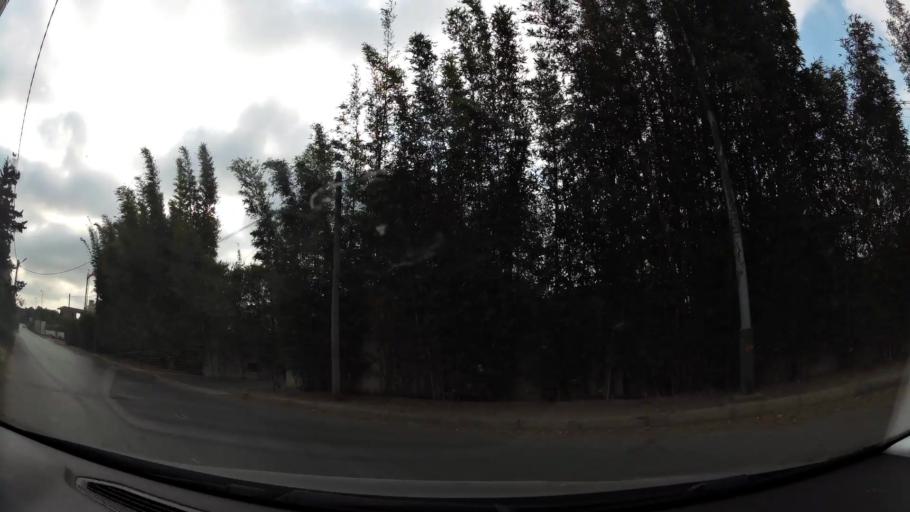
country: MA
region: Rabat-Sale-Zemmour-Zaer
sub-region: Rabat
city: Rabat
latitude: 33.9507
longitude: -6.8448
